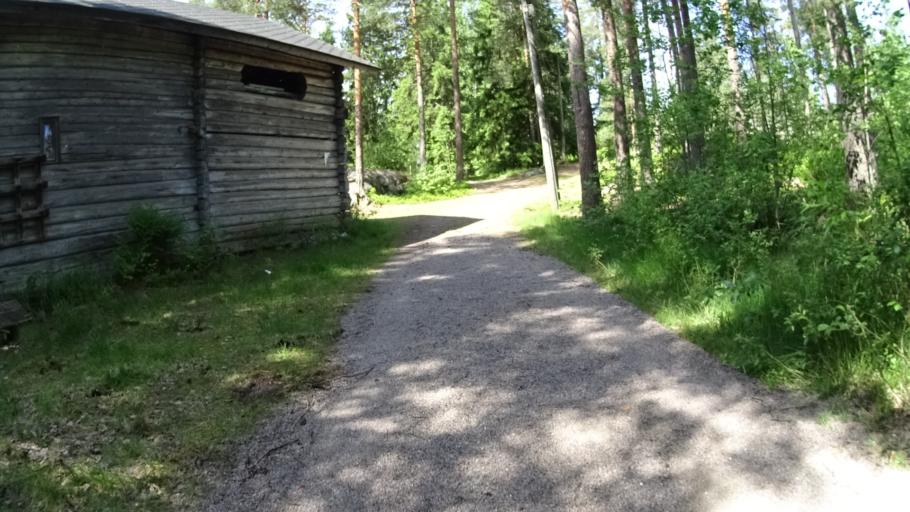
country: FI
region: Uusimaa
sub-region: Helsinki
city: Kauniainen
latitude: 60.3272
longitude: 24.7289
